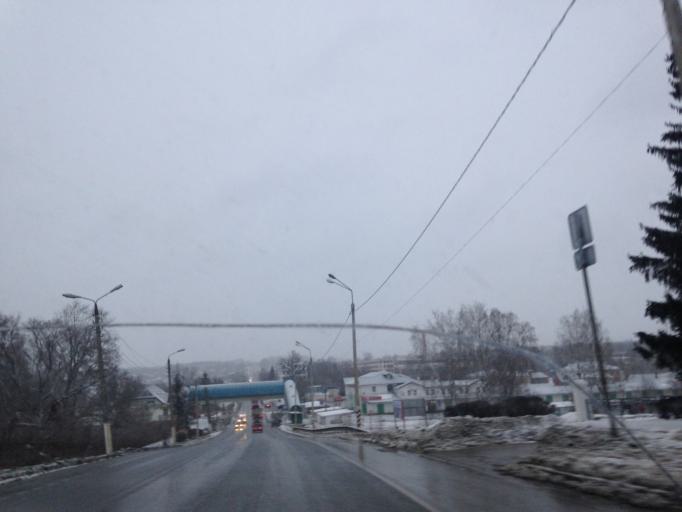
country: RU
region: Tula
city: Plavsk
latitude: 53.7084
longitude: 37.2946
